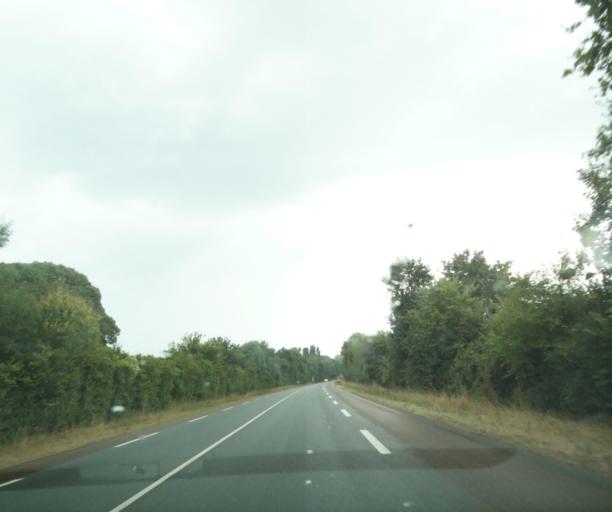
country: FR
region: Poitou-Charentes
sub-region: Departement de la Charente-Maritime
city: Cabariot
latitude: 45.9442
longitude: -0.8647
